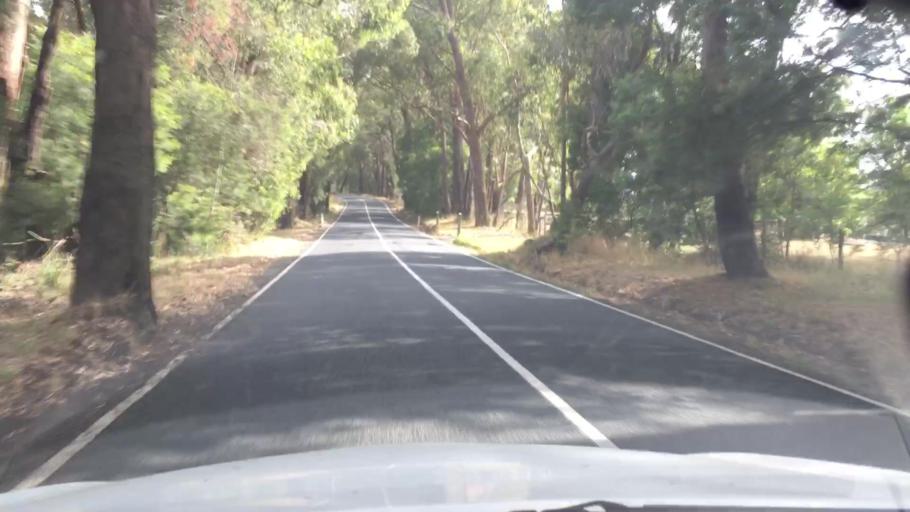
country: AU
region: Victoria
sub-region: Yarra Ranges
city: Macclesfield
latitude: -37.8423
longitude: 145.4862
